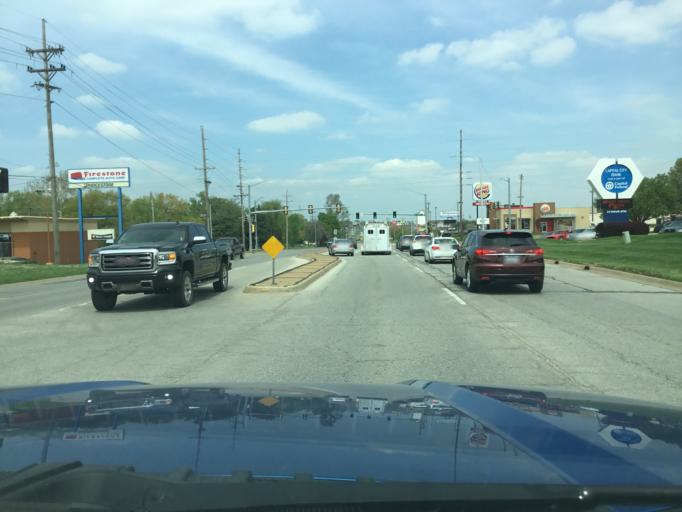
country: US
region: Kansas
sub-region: Shawnee County
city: Topeka
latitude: 38.9996
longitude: -95.6876
